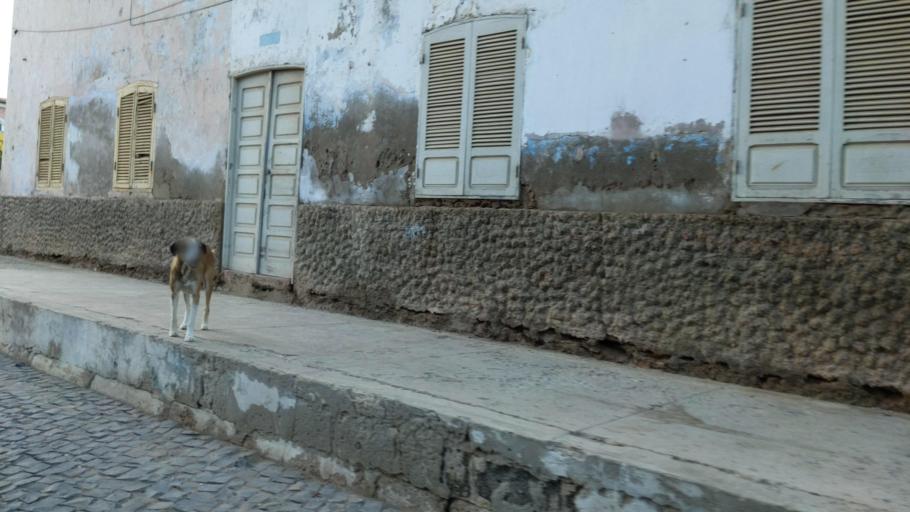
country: CV
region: Sal
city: Santa Maria
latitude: 16.5977
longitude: -22.9039
